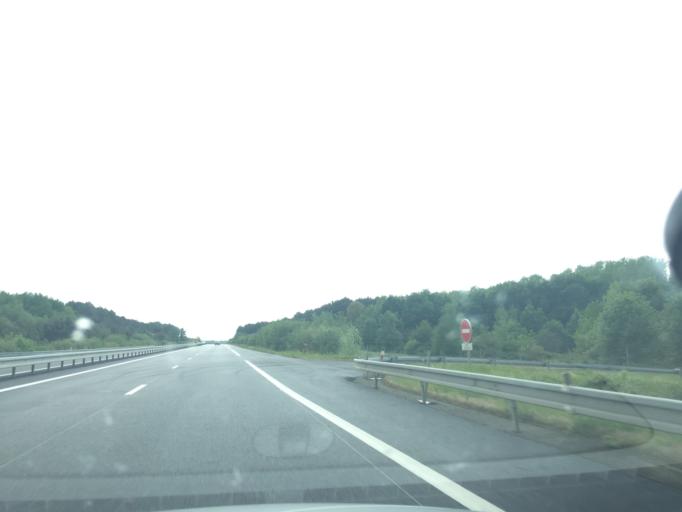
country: FR
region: Pays de la Loire
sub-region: Departement de la Sarthe
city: Brette-les-Pins
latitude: 47.9522
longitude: 0.3230
